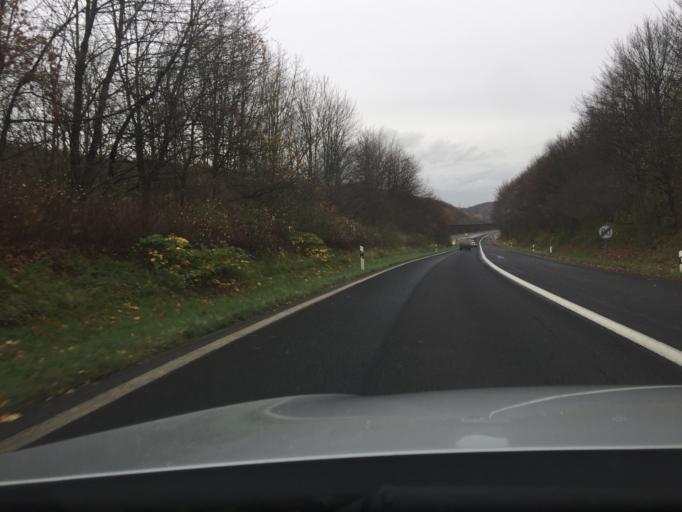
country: DE
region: North Rhine-Westphalia
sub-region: Regierungsbezirk Dusseldorf
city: Velbert
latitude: 51.3528
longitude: 7.0419
